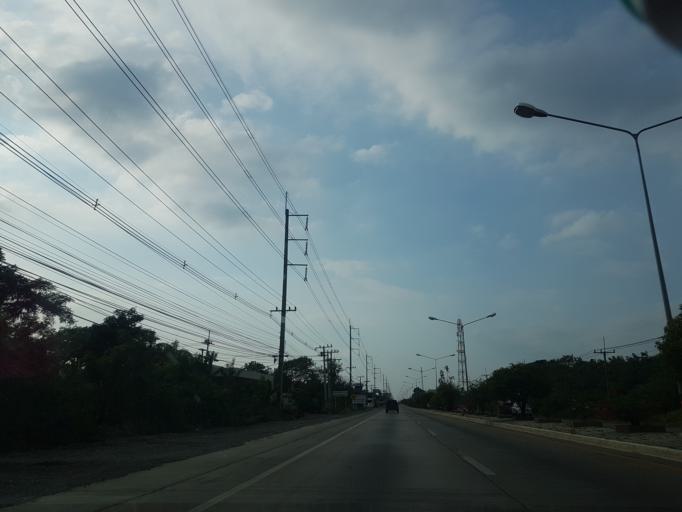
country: TH
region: Sara Buri
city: Phra Phutthabat
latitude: 14.7587
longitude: 100.7275
